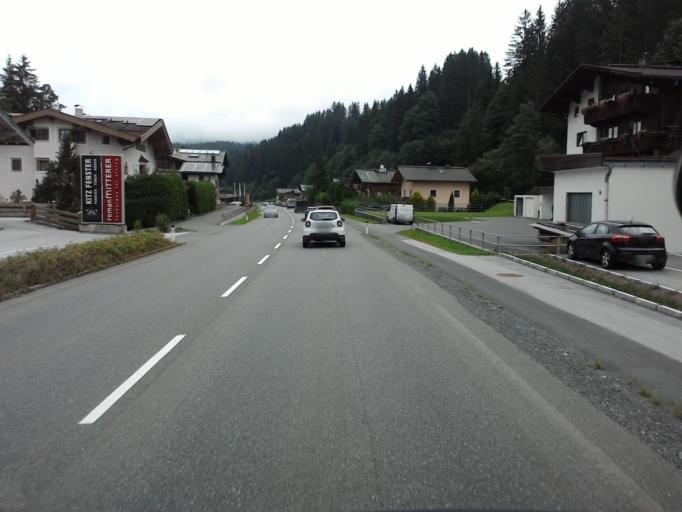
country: AT
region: Tyrol
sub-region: Politischer Bezirk Kitzbuhel
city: Jochberg
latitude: 47.4057
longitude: 12.4263
